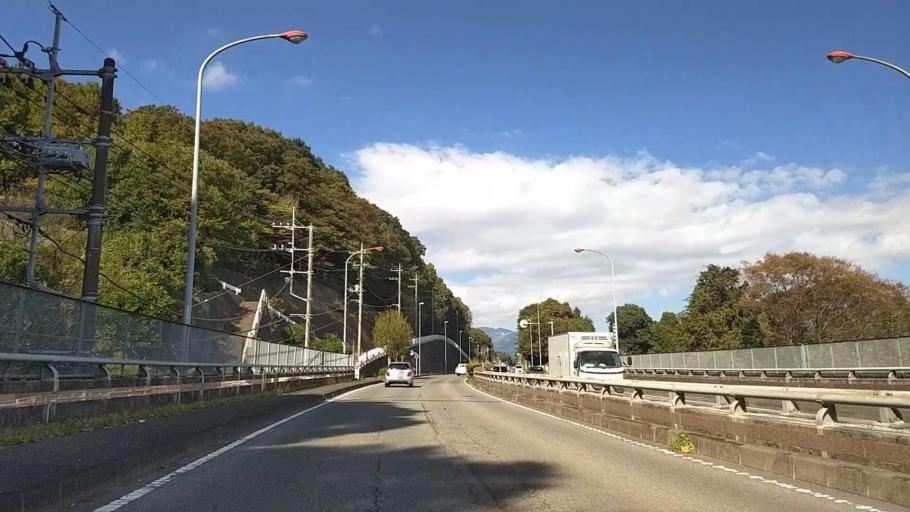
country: JP
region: Kanagawa
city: Ninomiya
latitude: 35.3284
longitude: 139.2330
